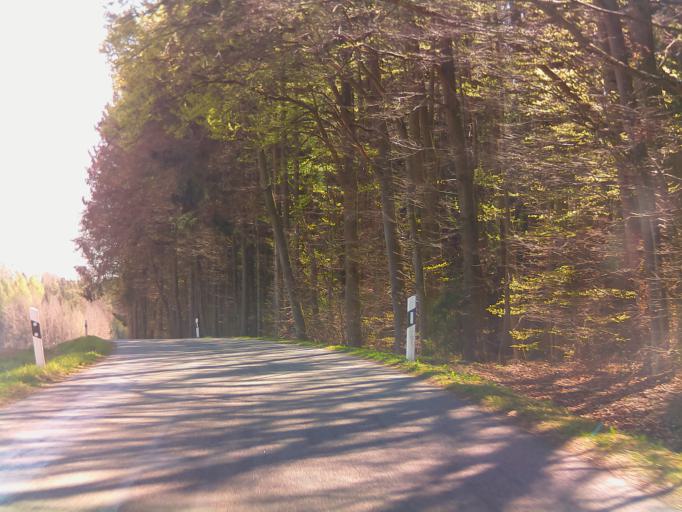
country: DE
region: Bavaria
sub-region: Upper Palatinate
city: Kastl
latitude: 49.4095
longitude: 11.6477
